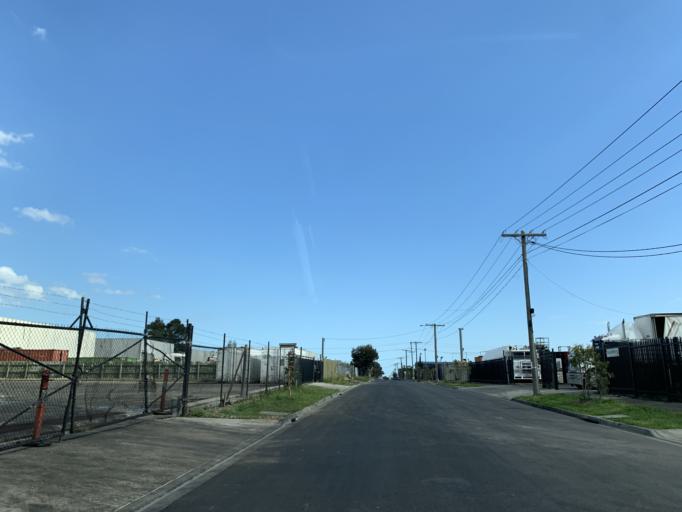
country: AU
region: Victoria
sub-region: Brimbank
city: Kealba
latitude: -37.7498
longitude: 144.8379
